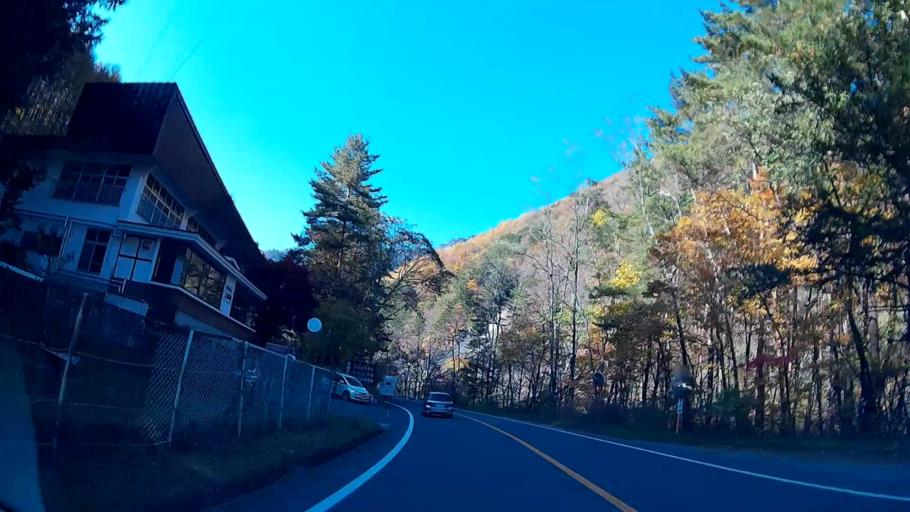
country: JP
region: Nagano
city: Toyoshina
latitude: 36.1683
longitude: 137.6509
